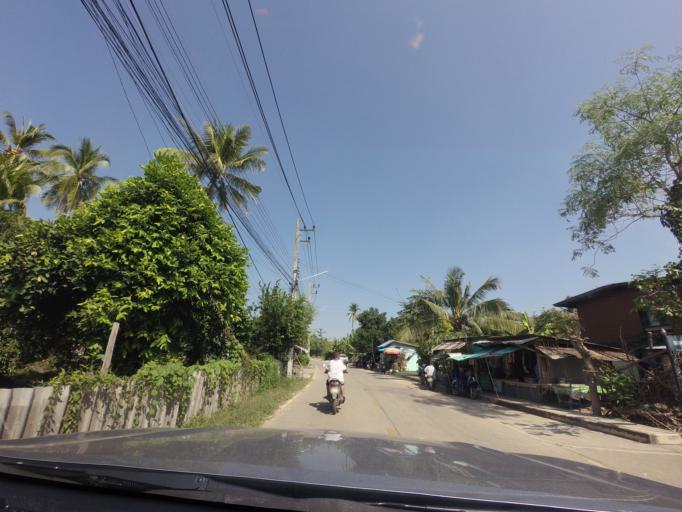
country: TH
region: Sukhothai
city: Sawankhalok
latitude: 17.3162
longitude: 99.8250
